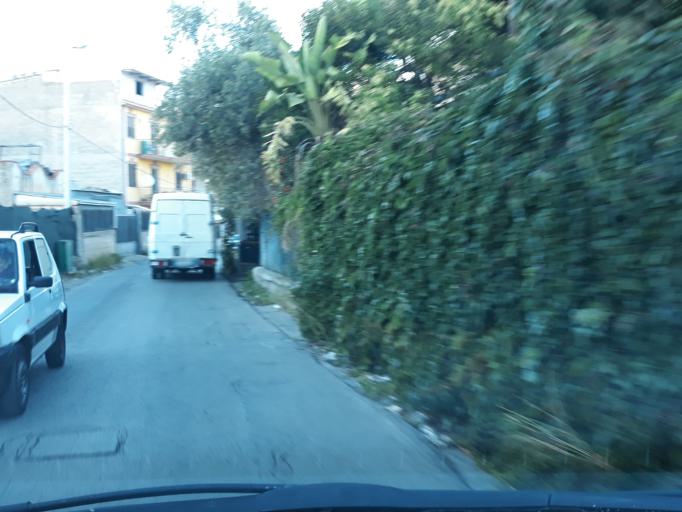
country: IT
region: Sicily
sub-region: Palermo
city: Villa Ciambra
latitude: 38.0772
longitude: 13.3122
